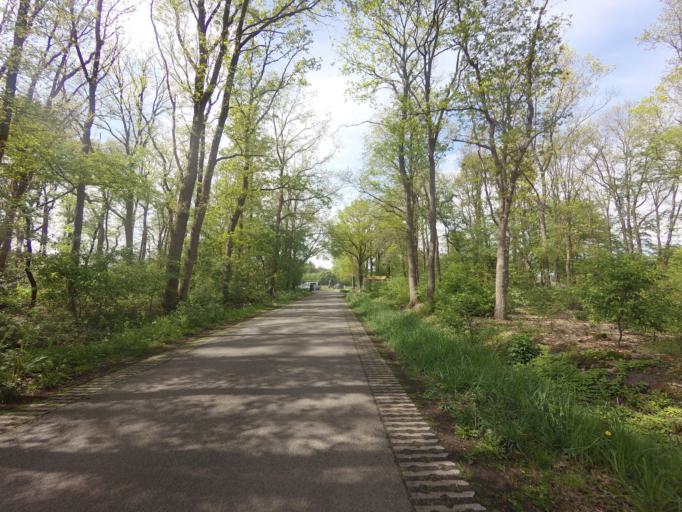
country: NL
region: Overijssel
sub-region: Gemeente Haaksbergen
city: Haaksbergen
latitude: 52.1385
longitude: 6.7290
